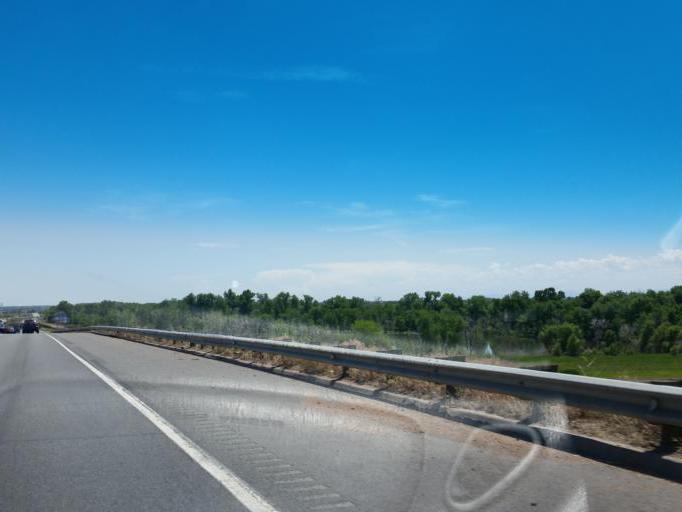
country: US
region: Colorado
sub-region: Larimer County
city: Fort Collins
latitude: 40.5391
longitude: -104.9959
